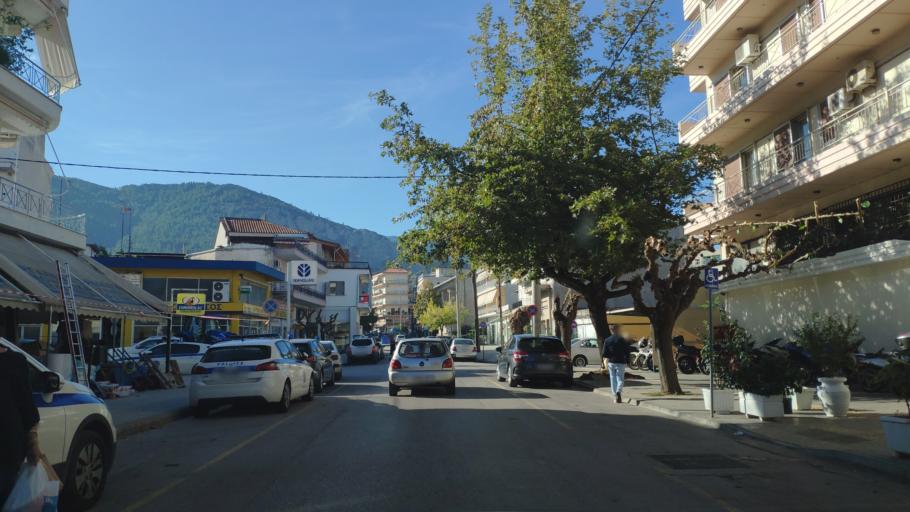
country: GR
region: Central Greece
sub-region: Nomos Voiotias
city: Livadeia
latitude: 38.4418
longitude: 22.8781
